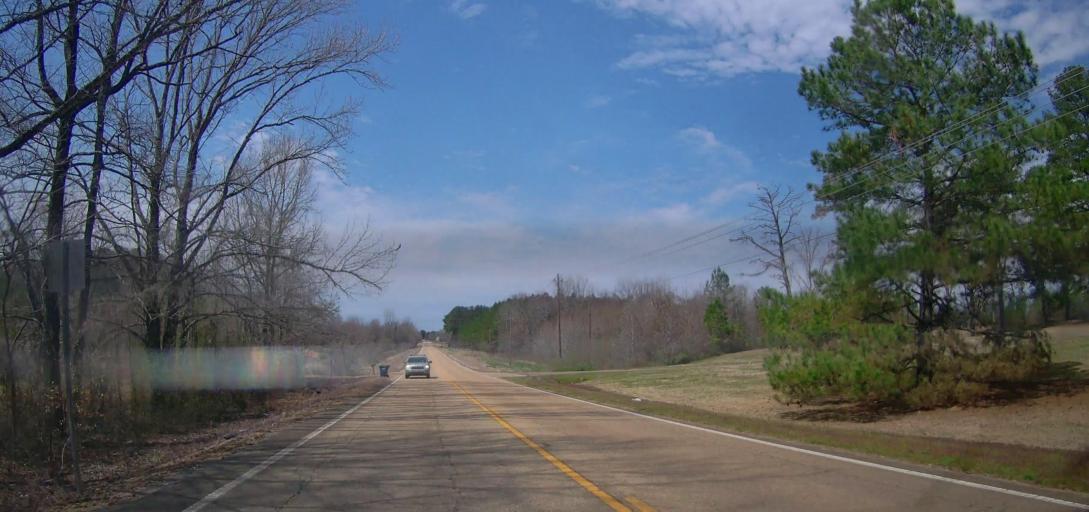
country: US
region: Mississippi
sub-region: Union County
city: New Albany
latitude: 34.6143
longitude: -89.1560
